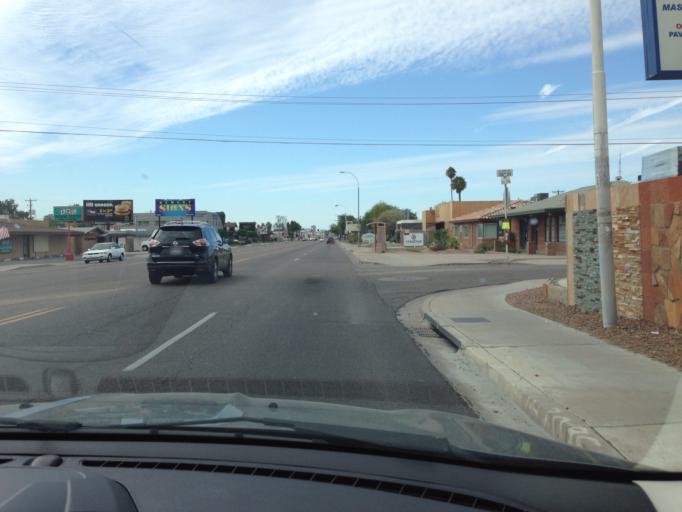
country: US
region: Arizona
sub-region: Maricopa County
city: Phoenix
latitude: 33.4950
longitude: -112.0257
